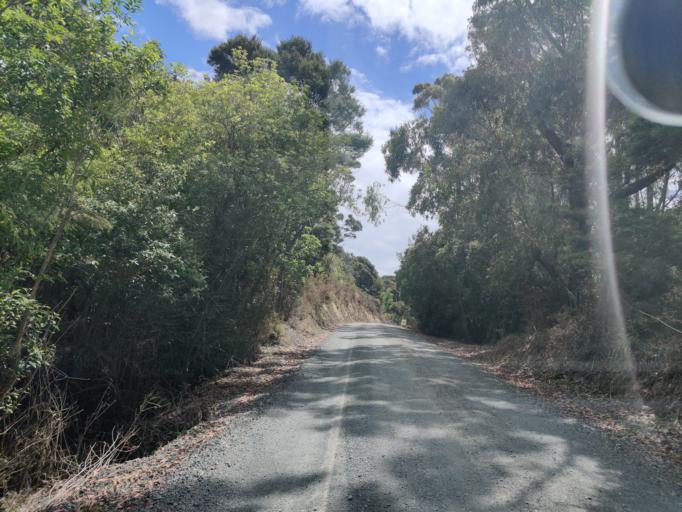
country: NZ
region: Northland
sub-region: Far North District
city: Paihia
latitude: -35.2596
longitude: 174.0591
